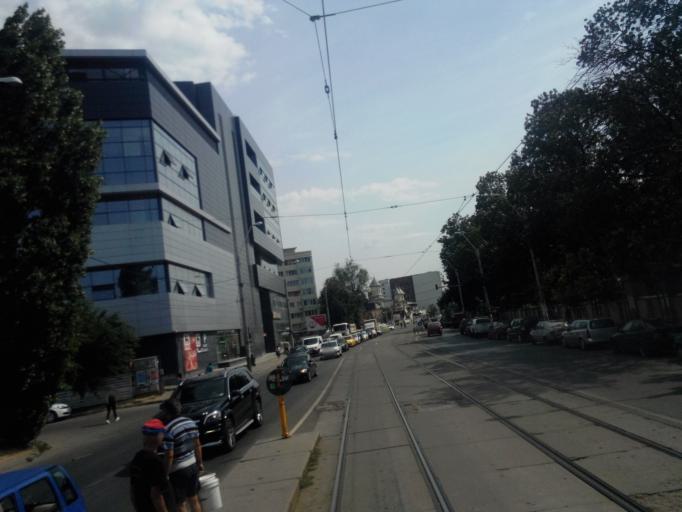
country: RO
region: Bucuresti
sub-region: Municipiul Bucuresti
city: Bucuresti
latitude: 44.4022
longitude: 26.0973
